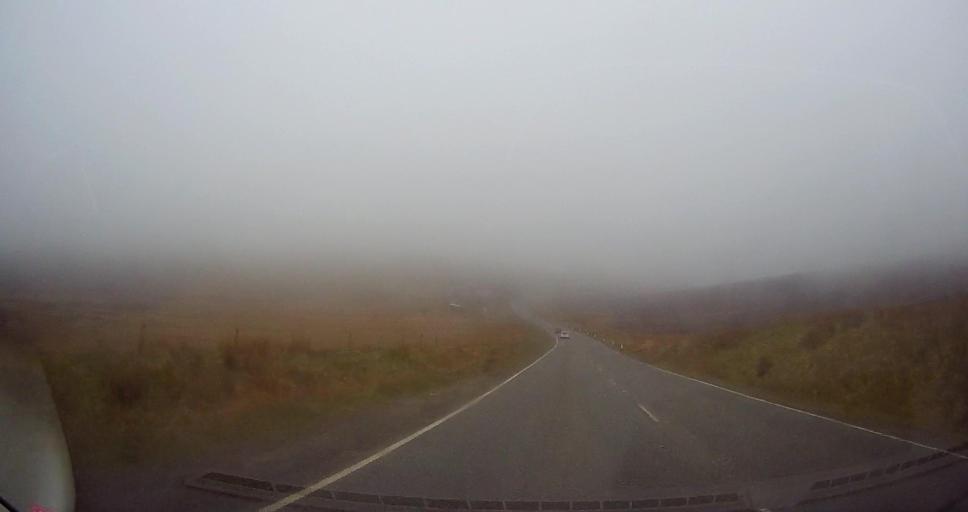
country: GB
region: Scotland
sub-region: Shetland Islands
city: Lerwick
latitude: 60.1419
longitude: -1.2451
